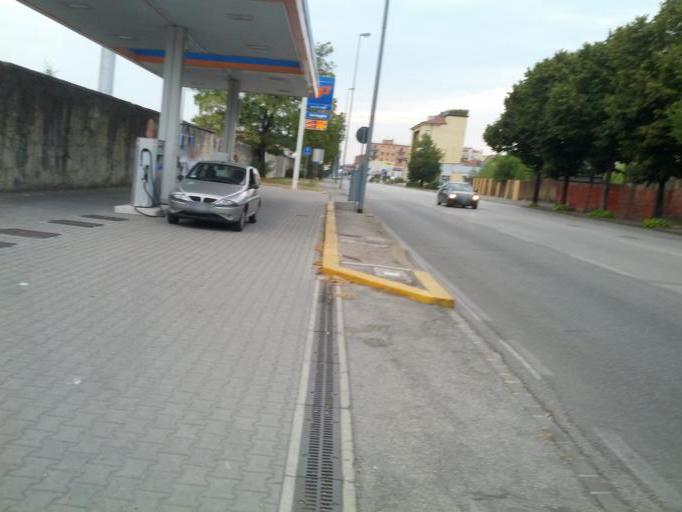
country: IT
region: Veneto
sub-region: Provincia di Verona
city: Poiano
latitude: 45.4376
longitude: 11.0251
